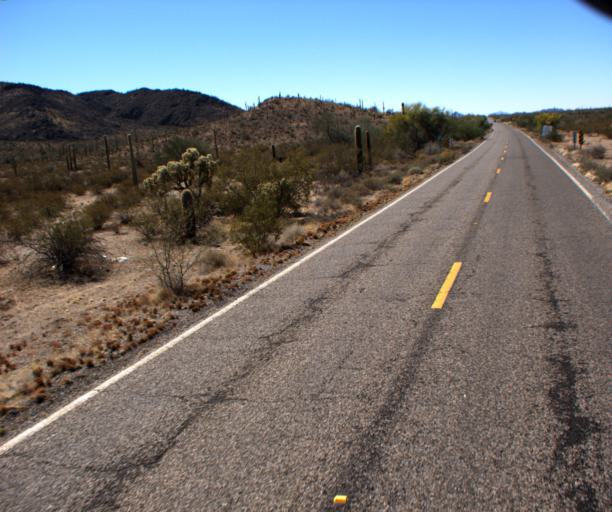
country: US
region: Arizona
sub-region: Pima County
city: Ajo
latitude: 32.2196
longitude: -112.7571
